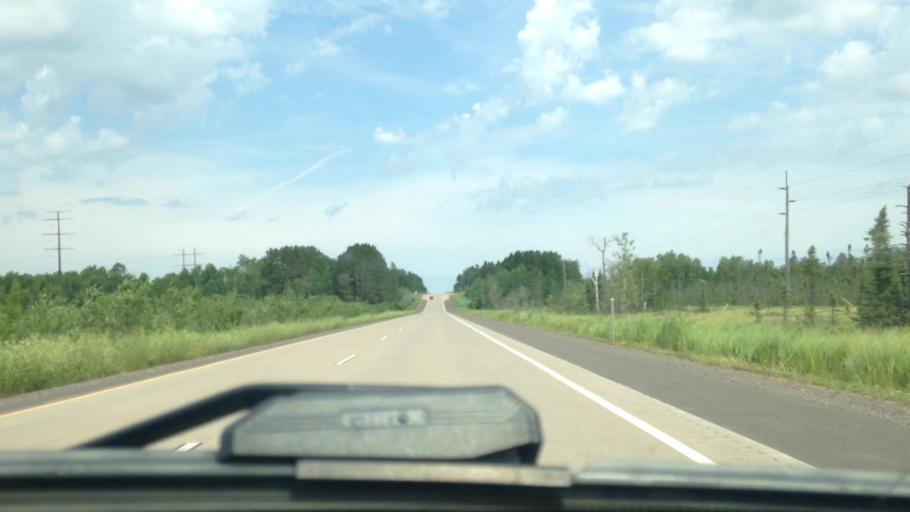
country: US
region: Wisconsin
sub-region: Douglas County
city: Lake Nebagamon
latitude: 46.2685
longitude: -91.8029
